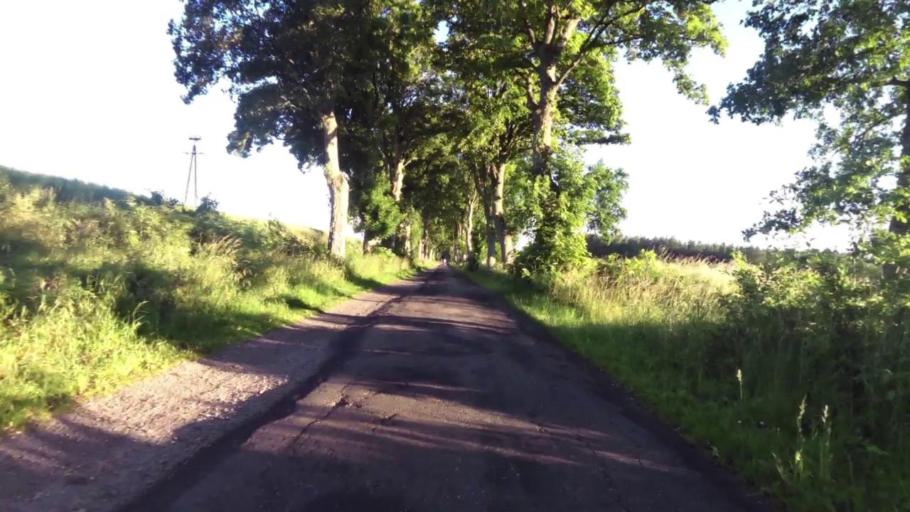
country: PL
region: West Pomeranian Voivodeship
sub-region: Koszalin
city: Koszalin
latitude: 54.0703
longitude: 16.1252
